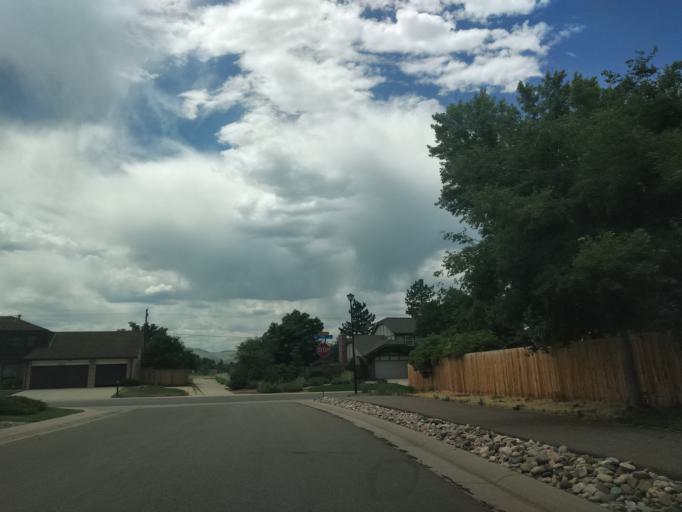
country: US
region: Colorado
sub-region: Jefferson County
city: Lakewood
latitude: 39.6763
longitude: -105.1040
